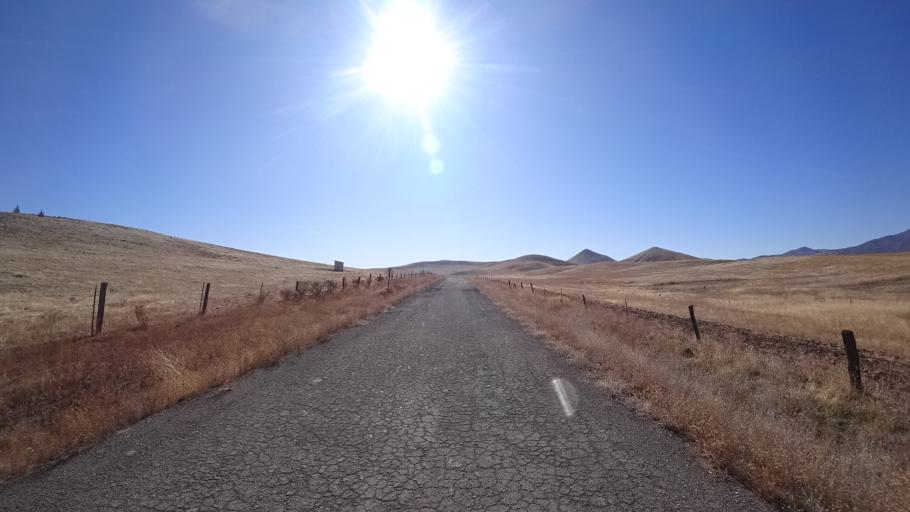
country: US
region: California
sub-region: Siskiyou County
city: Montague
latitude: 41.8467
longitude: -122.4595
